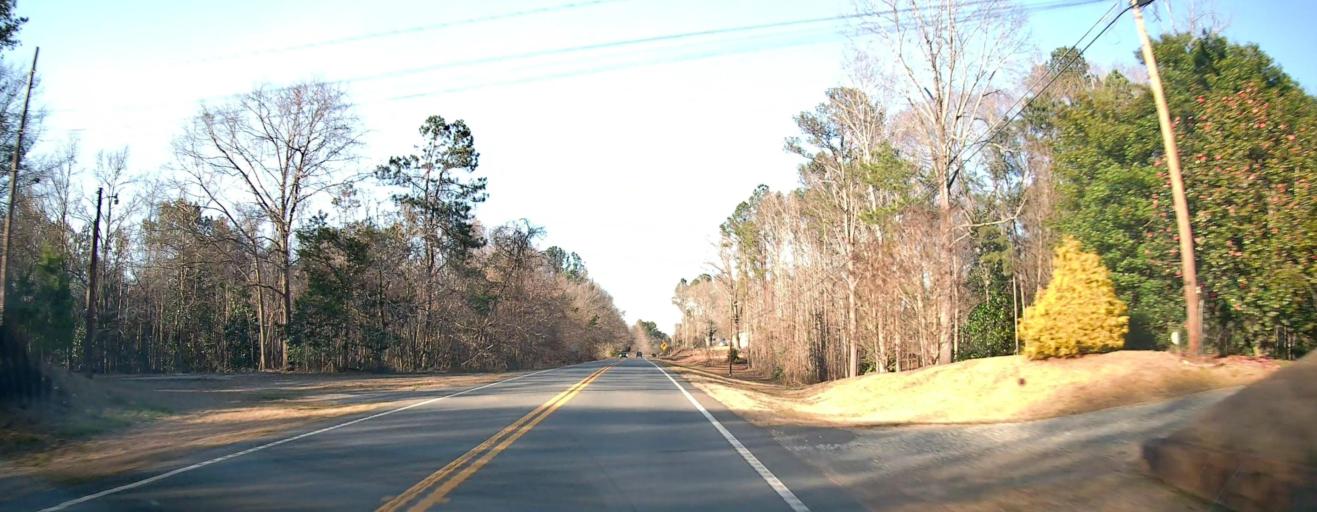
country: US
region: Georgia
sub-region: Meriwether County
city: Manchester
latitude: 32.8973
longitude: -84.6809
